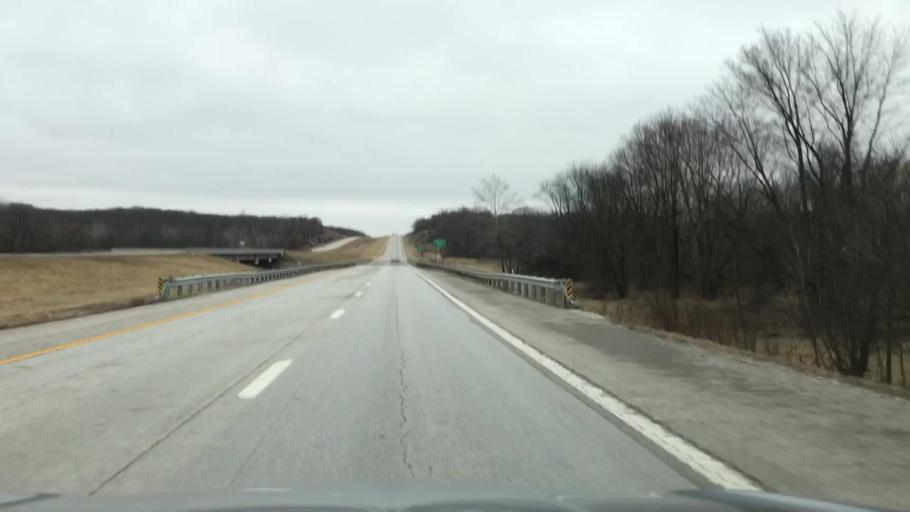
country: US
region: Missouri
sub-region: Linn County
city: Marceline
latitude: 39.7590
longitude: -92.8579
